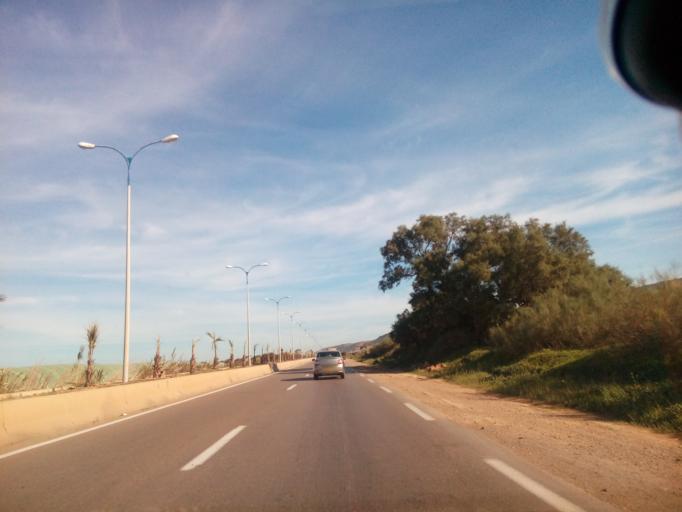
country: DZ
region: Mostaganem
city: Mostaganem
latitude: 35.8445
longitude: 0.0151
